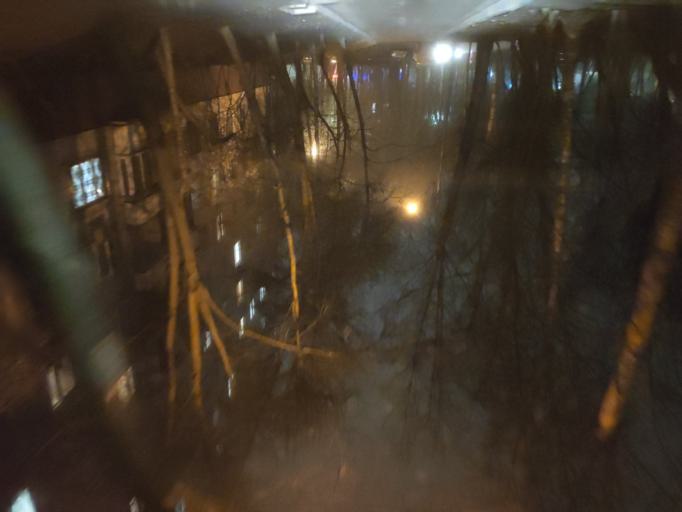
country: RU
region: Moscow
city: Yasenevo
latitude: 55.6061
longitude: 37.5194
